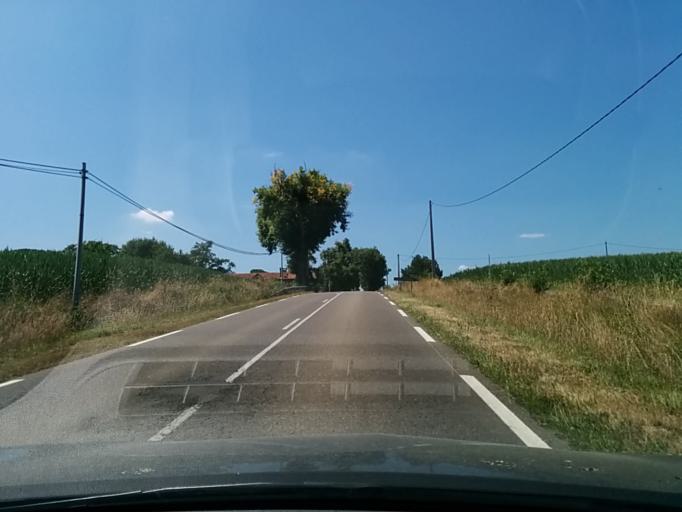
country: FR
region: Midi-Pyrenees
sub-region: Departement du Gers
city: Le Houga
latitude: 43.7604
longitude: -0.1069
